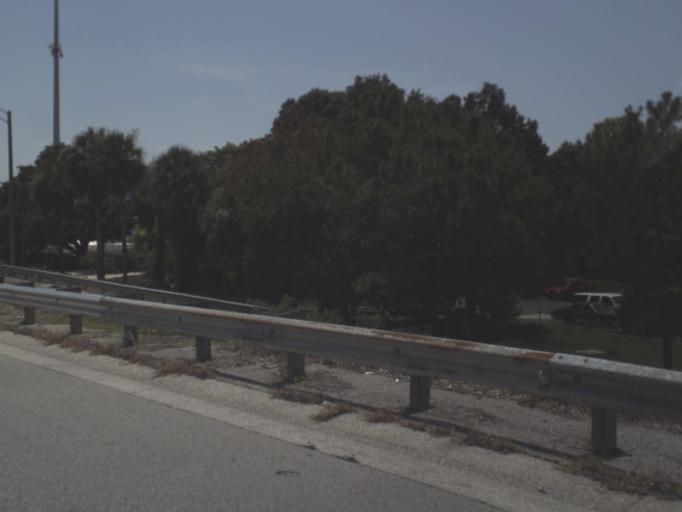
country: US
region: Florida
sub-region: Pinellas County
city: Saint Petersburg
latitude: 27.7907
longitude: -82.6607
